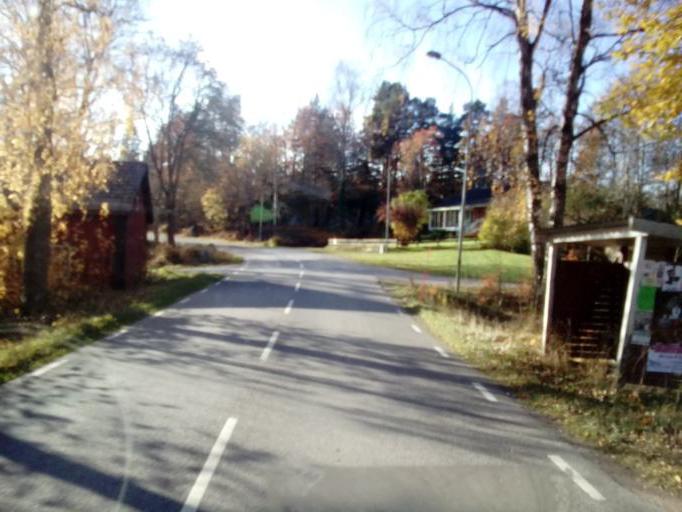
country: SE
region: Kalmar
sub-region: Vimmerby Kommun
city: Vimmerby
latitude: 57.7207
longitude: 16.0684
